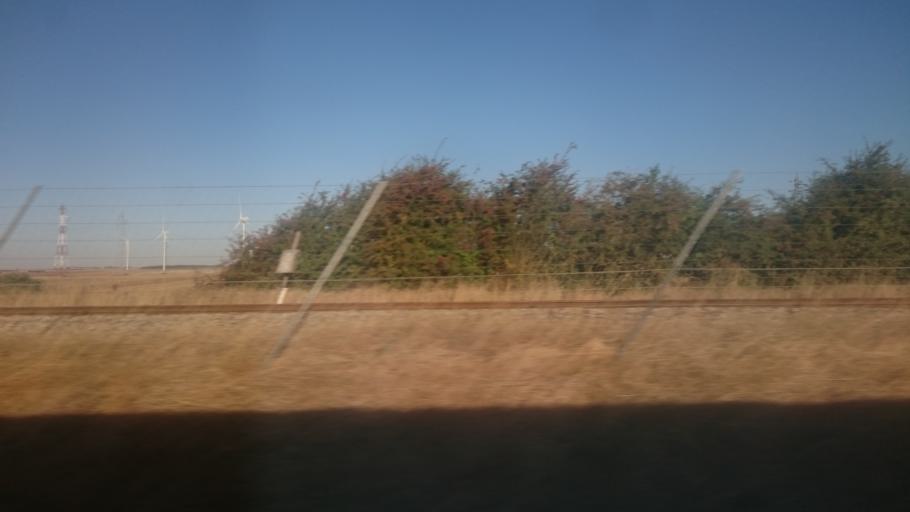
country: FR
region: Centre
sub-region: Departement d'Eure-et-Loir
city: Voves
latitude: 48.3211
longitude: 1.6679
